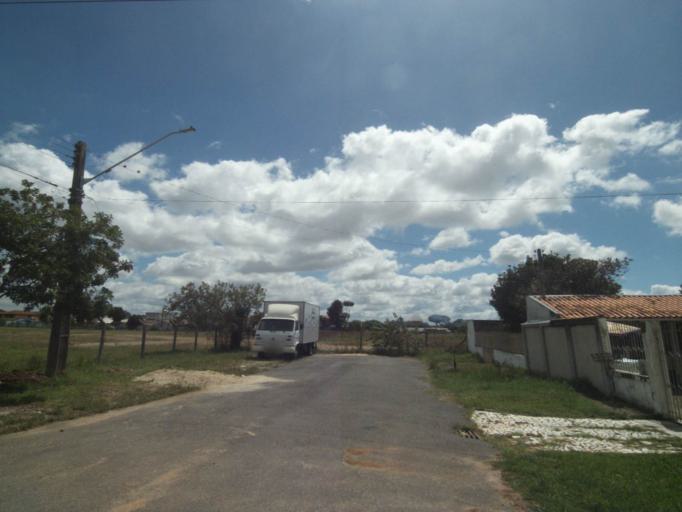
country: BR
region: Parana
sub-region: Pinhais
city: Pinhais
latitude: -25.4402
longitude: -49.2047
